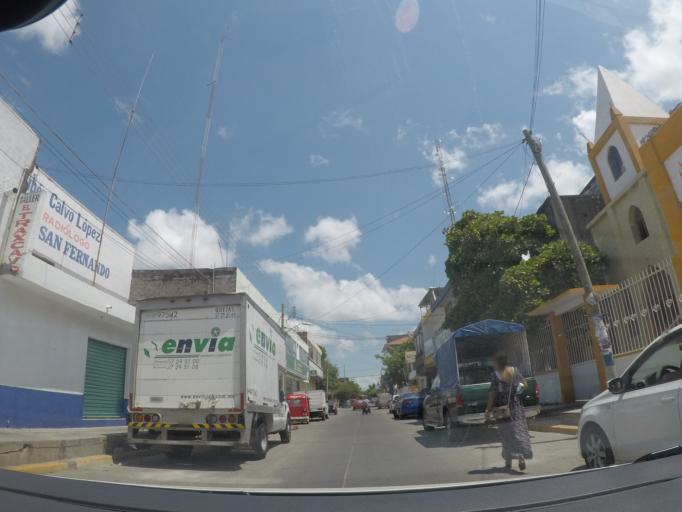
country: MX
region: Oaxaca
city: Juchitan de Zaragoza
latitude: 16.4414
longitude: -95.0221
